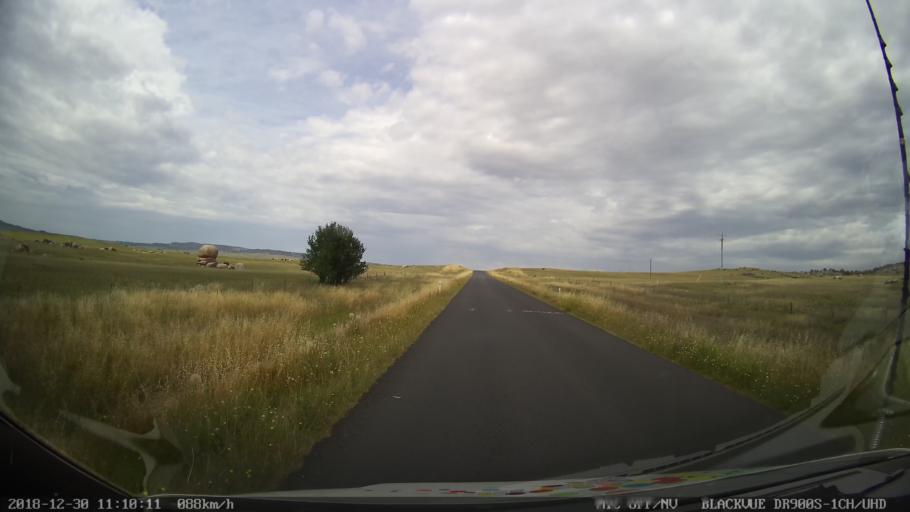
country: AU
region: New South Wales
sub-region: Snowy River
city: Berridale
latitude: -36.5125
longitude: 148.7842
